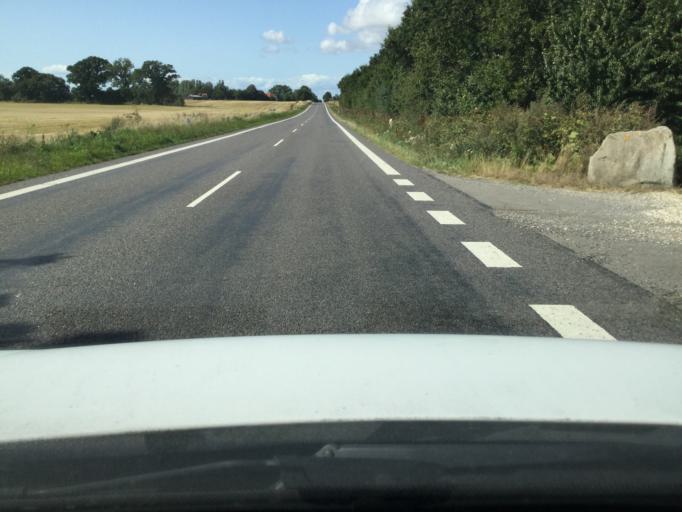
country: DK
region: Zealand
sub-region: Lolland Kommune
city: Rodby
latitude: 54.7867
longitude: 11.2884
